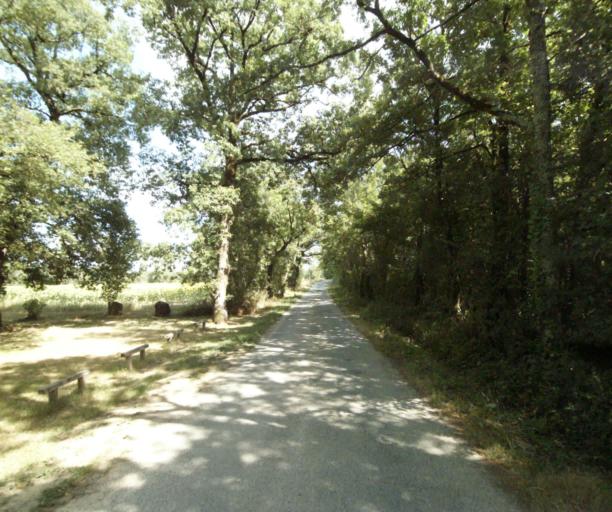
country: FR
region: Midi-Pyrenees
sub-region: Departement du Tarn
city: Puylaurens
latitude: 43.5150
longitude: 2.0394
